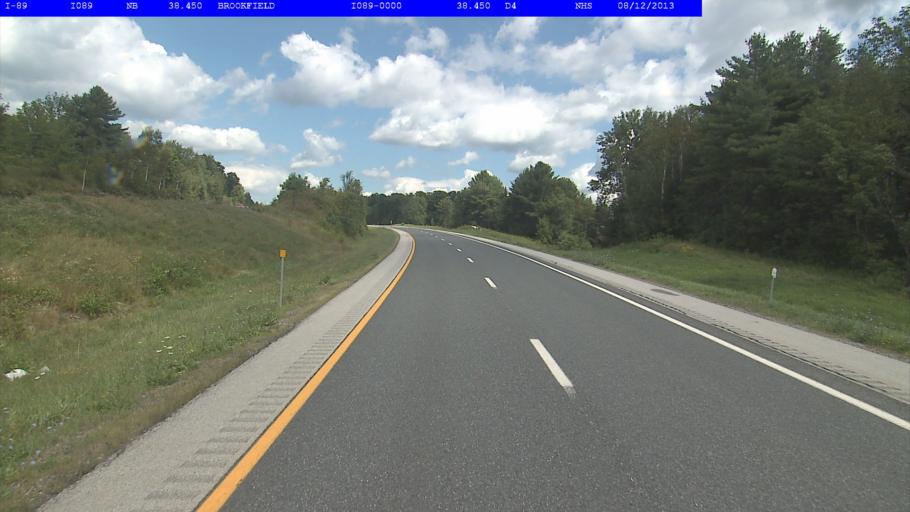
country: US
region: Vermont
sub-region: Orange County
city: Williamstown
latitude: 44.0515
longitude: -72.6047
